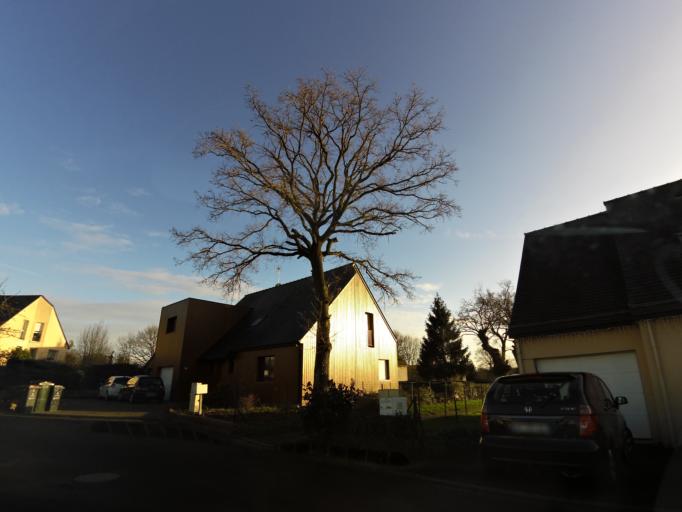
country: FR
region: Brittany
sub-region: Departement d'Ille-et-Vilaine
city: Pance
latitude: 47.8980
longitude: -1.6090
